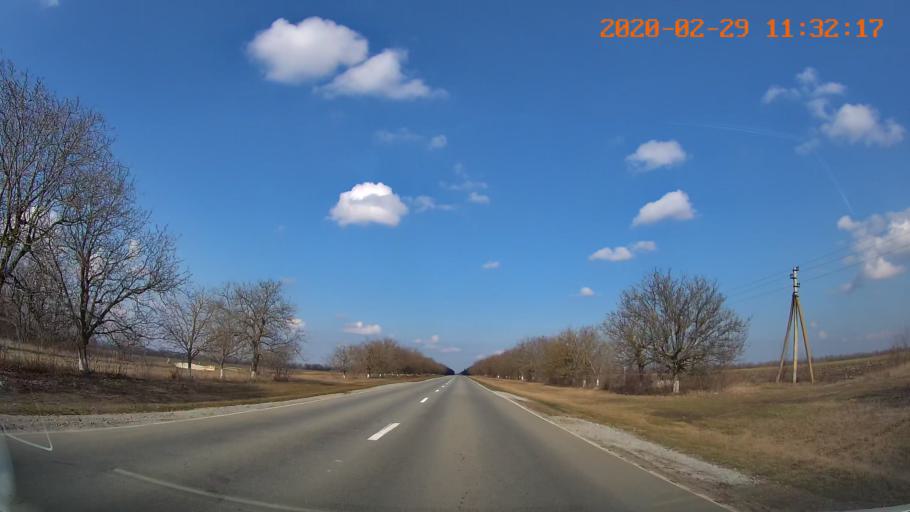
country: MD
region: Rezina
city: Saharna
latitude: 47.5359
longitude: 29.0960
